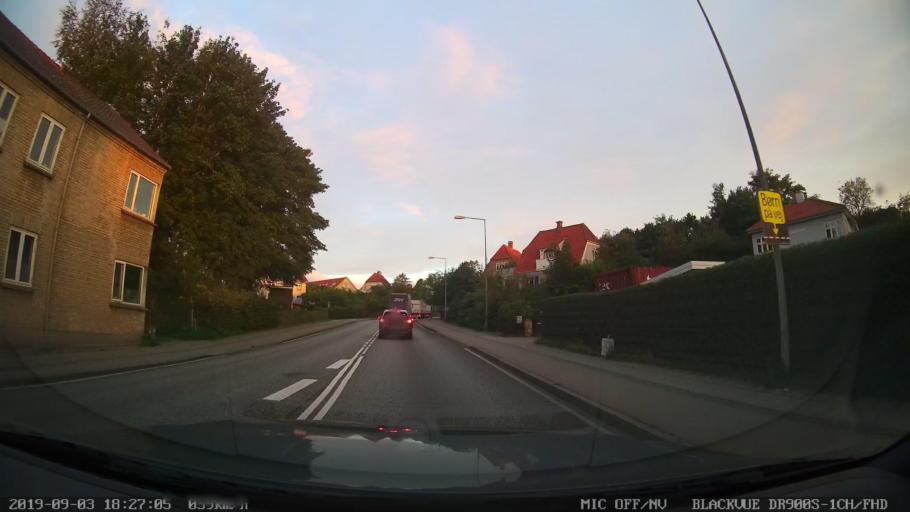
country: DK
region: Capital Region
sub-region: Helsingor Kommune
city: Helsingor
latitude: 56.0287
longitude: 12.6029
